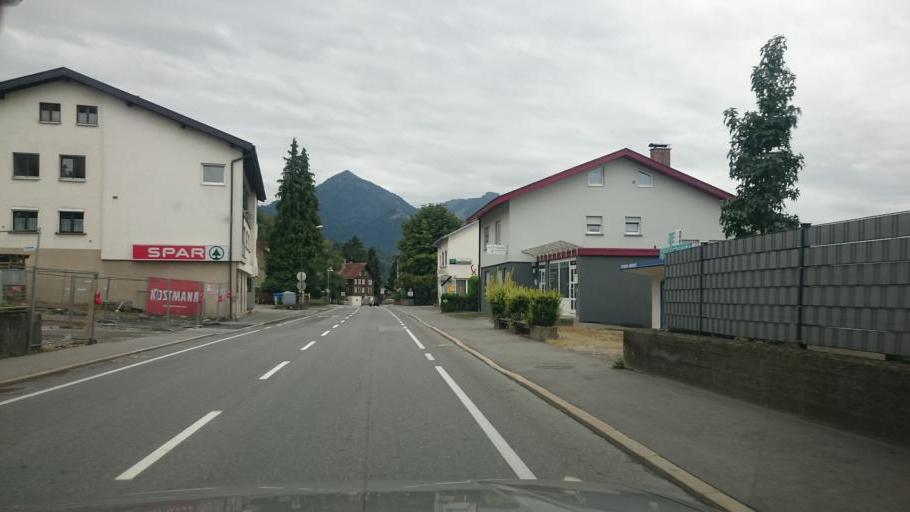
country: AT
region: Vorarlberg
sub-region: Politischer Bezirk Dornbirn
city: Dornbirn
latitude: 47.4289
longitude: 9.7552
